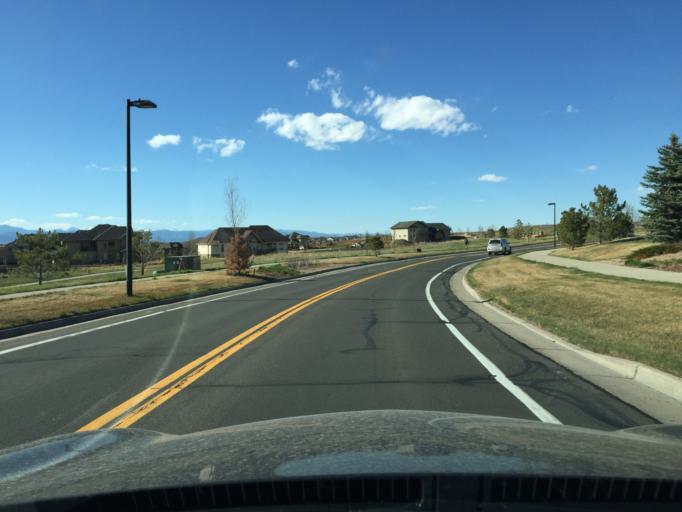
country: US
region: Colorado
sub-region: Boulder County
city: Erie
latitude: 40.0112
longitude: -105.0337
